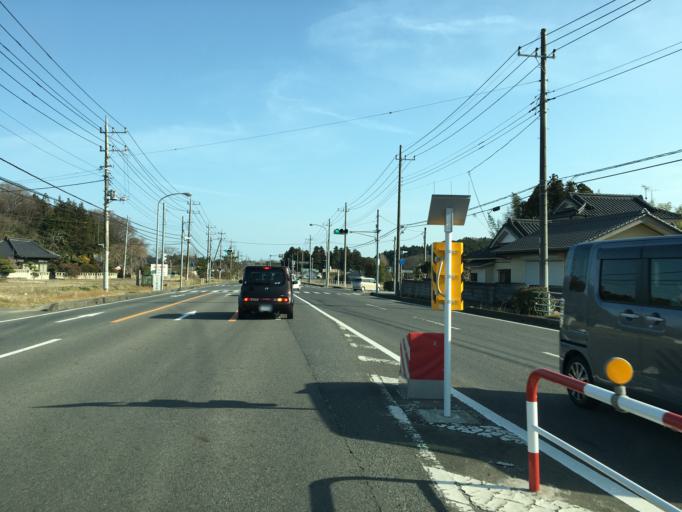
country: JP
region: Ibaraki
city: Takahagi
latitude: 36.7413
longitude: 140.6901
